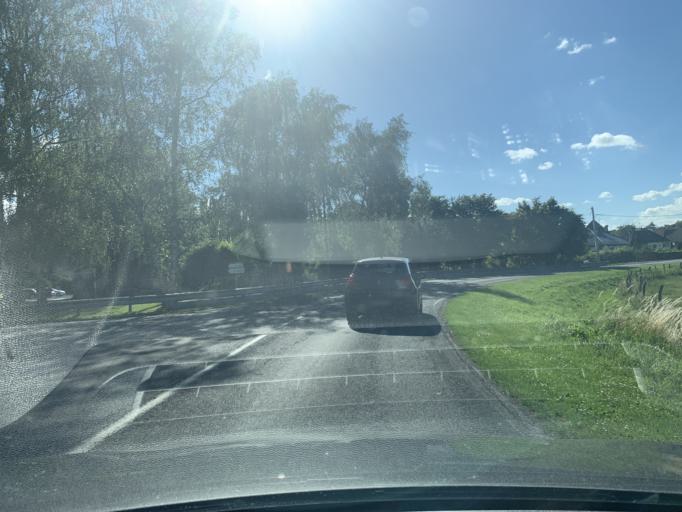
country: FR
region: Nord-Pas-de-Calais
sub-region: Departement du Nord
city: Lauwin-Planque
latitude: 50.3740
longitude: 3.0172
